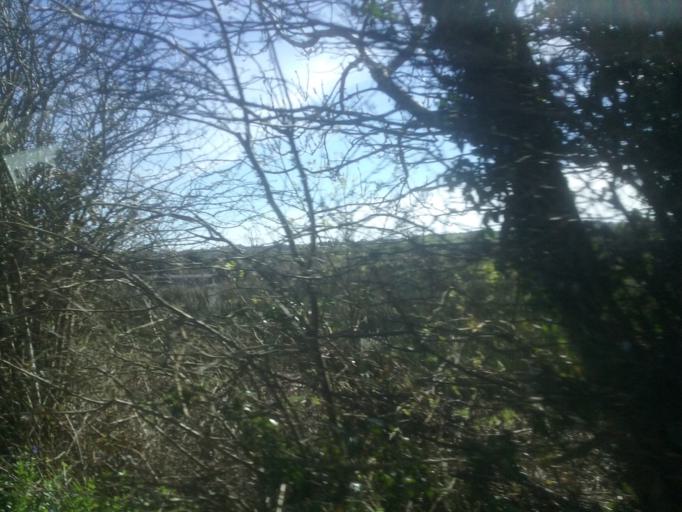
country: IE
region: Munster
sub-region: An Clar
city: Kilrush
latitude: 52.6700
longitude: -9.4958
